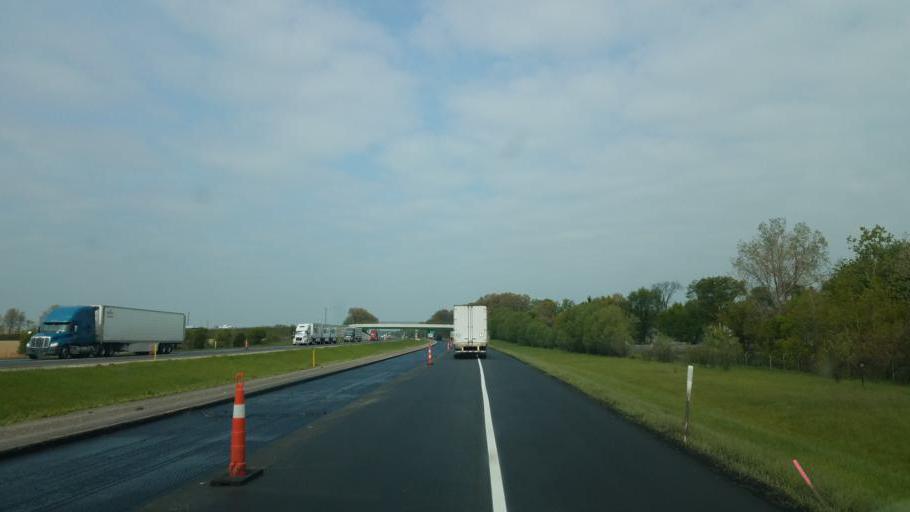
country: US
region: Indiana
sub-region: Saint Joseph County
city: Granger
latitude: 41.7336
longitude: -86.1064
